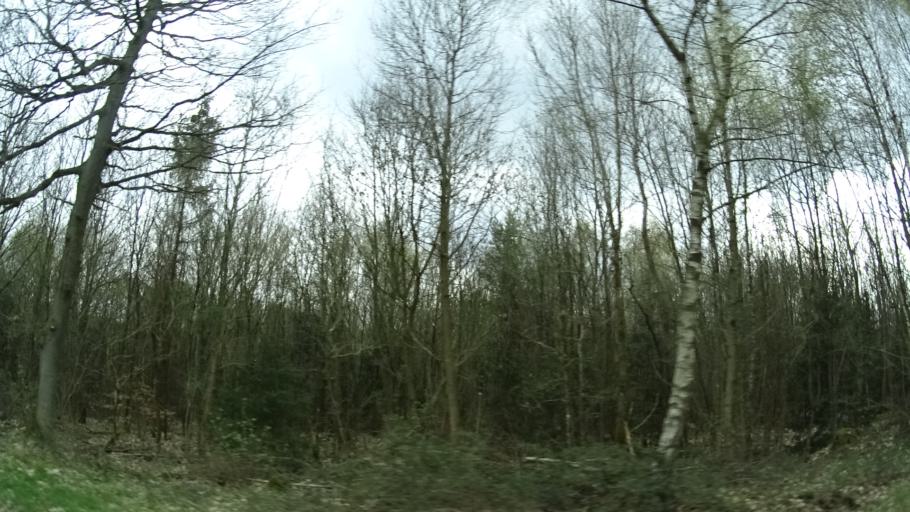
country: DE
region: Rheinland-Pfalz
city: Seesbach
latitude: 49.8653
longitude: 7.5759
